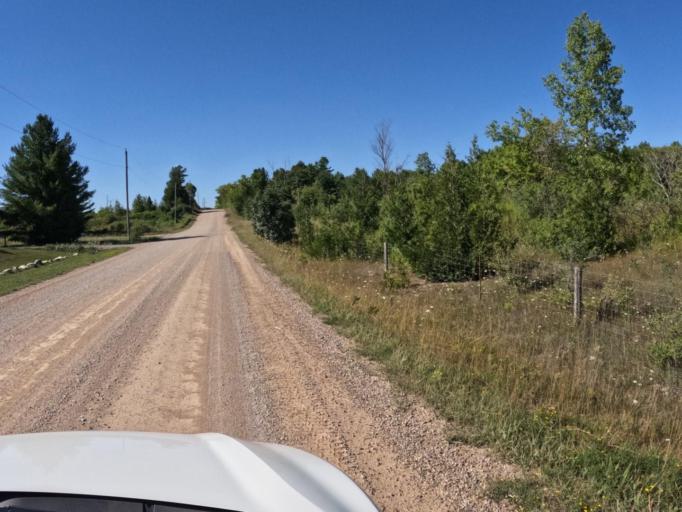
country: CA
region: Ontario
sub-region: Wellington County
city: Guelph
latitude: 43.4206
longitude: -80.1236
